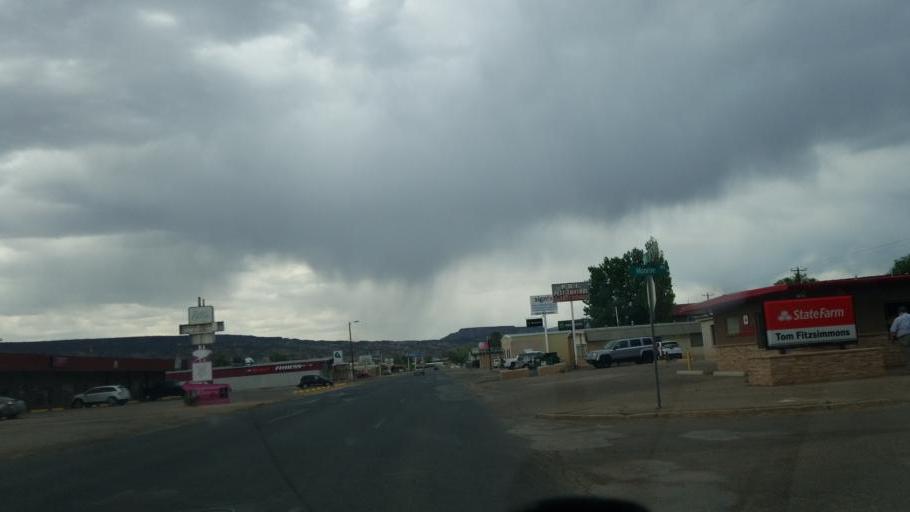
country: US
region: New Mexico
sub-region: Cibola County
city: Grants
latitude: 35.1569
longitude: -107.8444
